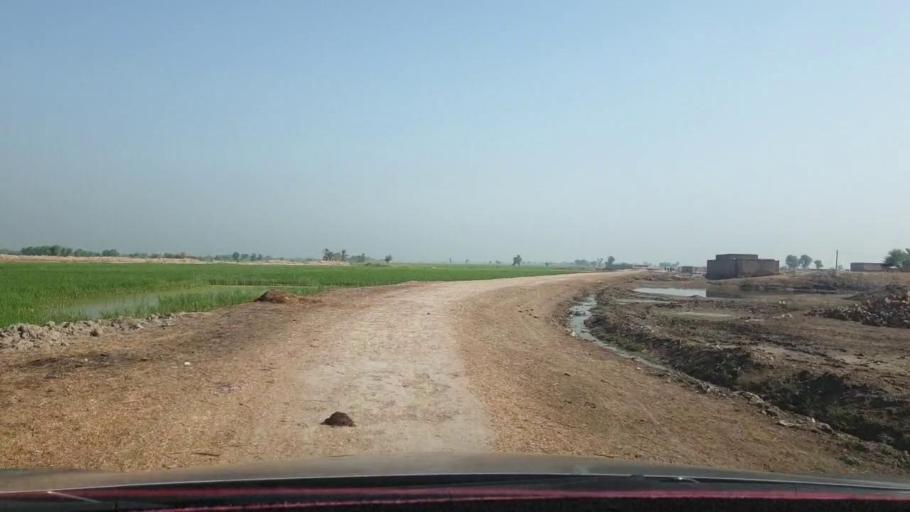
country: PK
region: Sindh
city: Nasirabad
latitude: 27.4622
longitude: 67.9188
